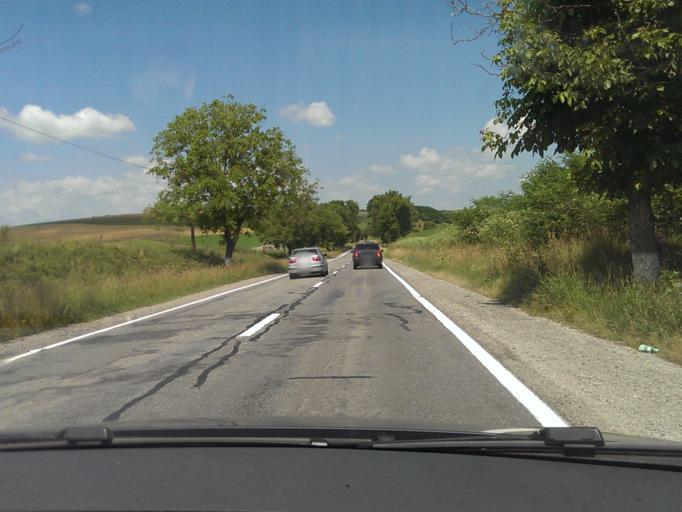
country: RO
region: Cluj
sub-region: Comuna Apahida
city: Apahida
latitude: 46.8047
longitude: 23.7719
